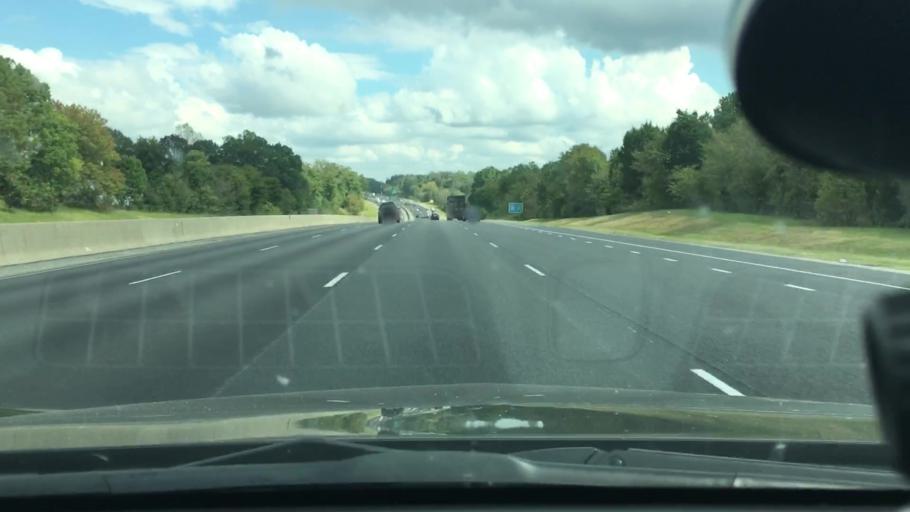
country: US
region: North Carolina
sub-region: Guilford County
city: Gibsonville
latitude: 36.0603
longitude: -79.6006
